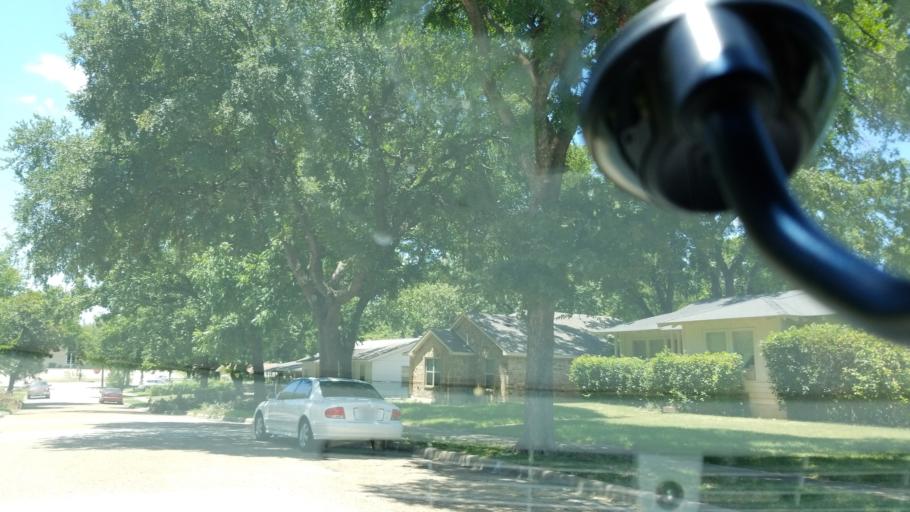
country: US
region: Texas
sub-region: Dallas County
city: Cockrell Hill
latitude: 32.6884
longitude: -96.8131
